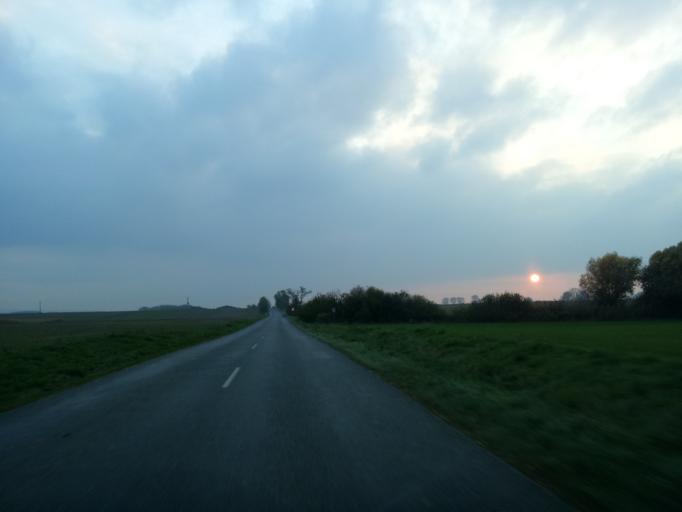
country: HU
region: Gyor-Moson-Sopron
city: Bakonyszentlaszlo
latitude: 47.4558
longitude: 17.8278
